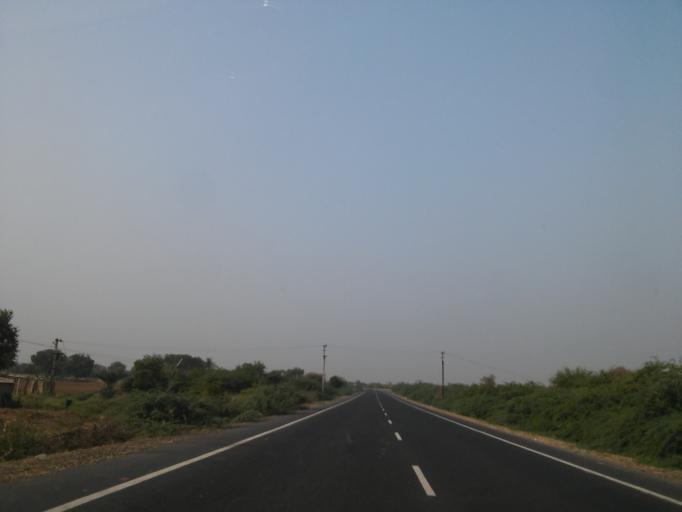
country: IN
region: Gujarat
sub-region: Kachchh
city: Anjar
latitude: 23.2855
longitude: 70.0012
